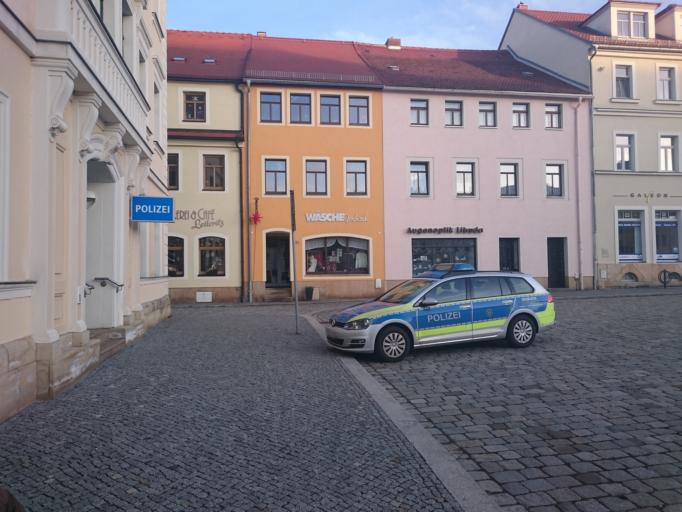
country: DE
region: Saxony
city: Dippoldiswalde
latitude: 50.8972
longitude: 13.6677
